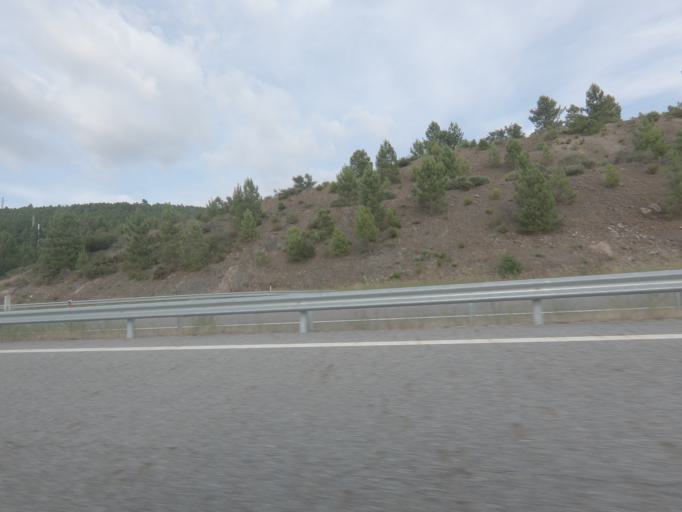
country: PT
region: Vila Real
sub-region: Boticas
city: Boticas
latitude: 41.6742
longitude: -7.5671
